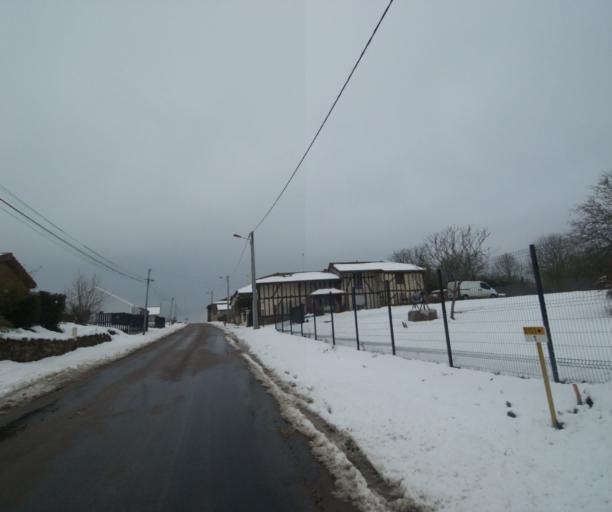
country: FR
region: Champagne-Ardenne
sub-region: Departement de la Haute-Marne
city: Laneuville-a-Remy
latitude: 48.5019
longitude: 4.8696
